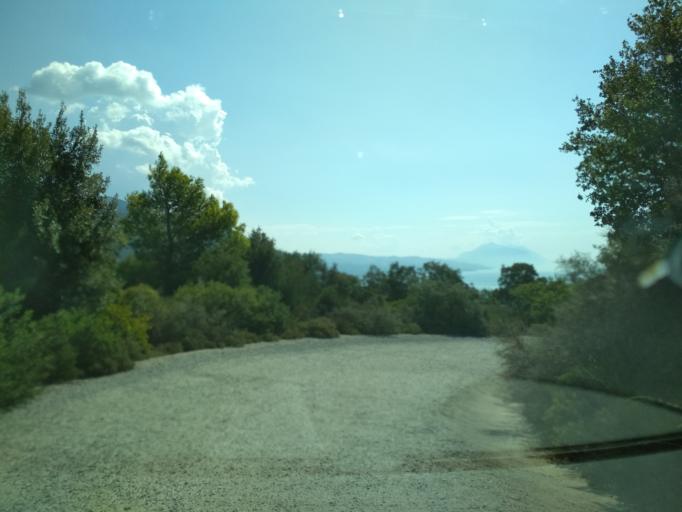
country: GR
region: Central Greece
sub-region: Nomos Evvoias
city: Oreoi
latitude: 38.8530
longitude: 23.1195
